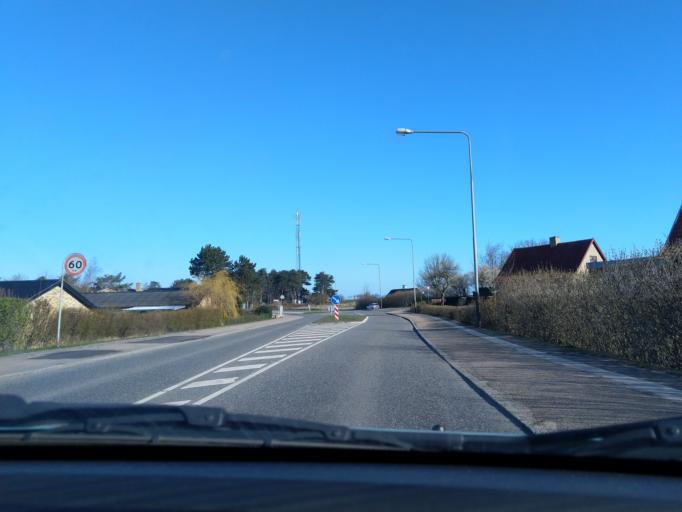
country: DK
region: Zealand
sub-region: Kalundborg Kommune
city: Kalundborg
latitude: 55.7101
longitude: 11.0209
